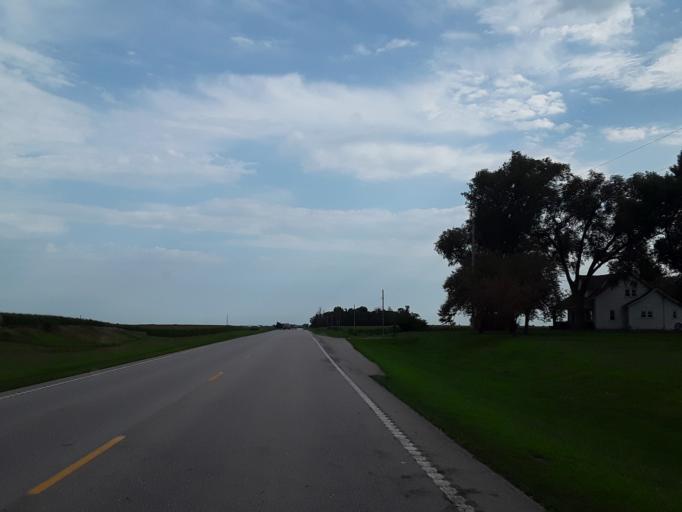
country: US
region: Nebraska
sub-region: Saunders County
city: Ashland
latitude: 41.1224
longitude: -96.4257
